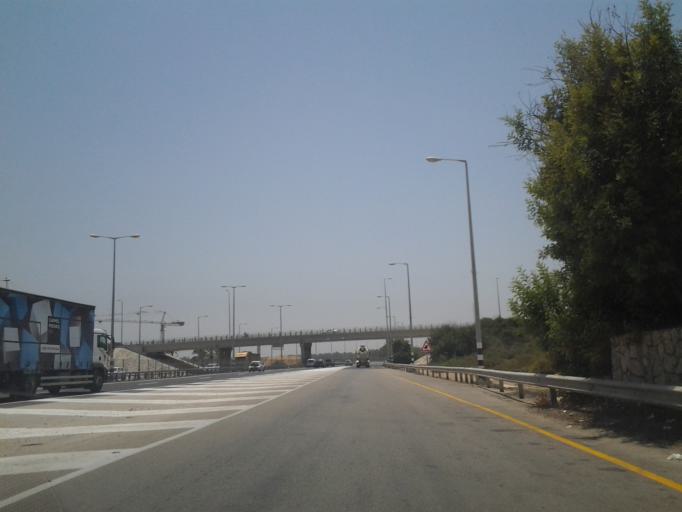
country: IL
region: Haifa
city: Hadera
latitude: 32.4453
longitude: 34.8925
